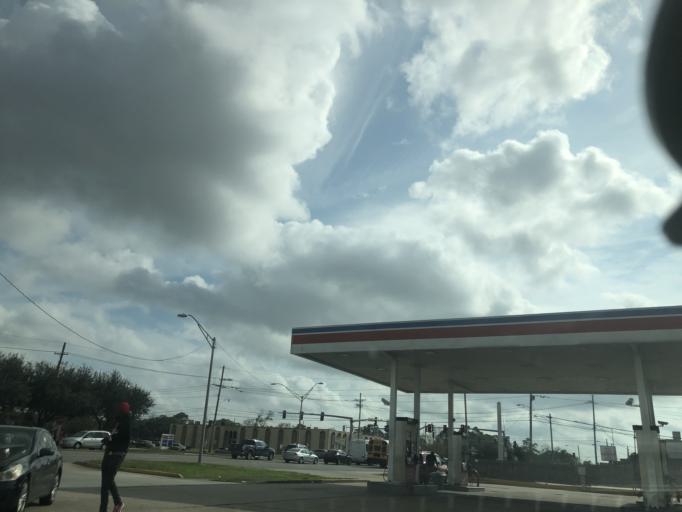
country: US
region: Louisiana
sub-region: Jefferson Parish
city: Metairie
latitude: 29.9932
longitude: -90.1561
